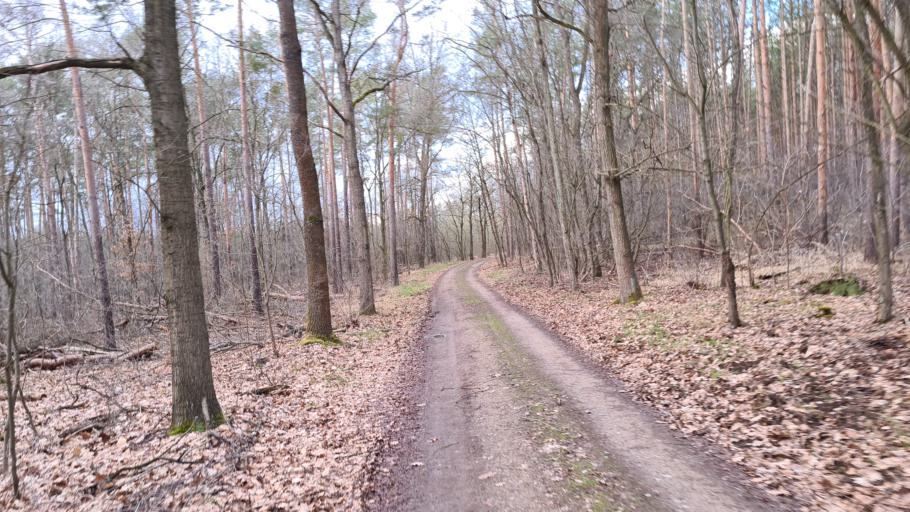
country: DE
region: Brandenburg
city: Falkenberg
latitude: 51.5839
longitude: 13.3061
